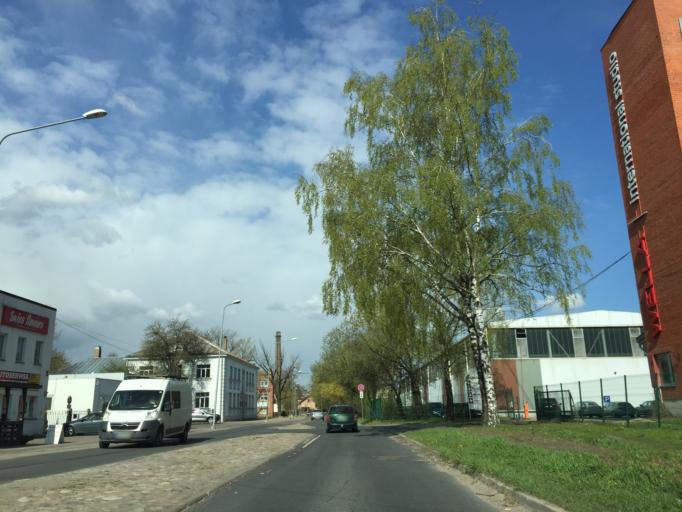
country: LV
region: Riga
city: Riga
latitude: 56.9285
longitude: 24.1028
